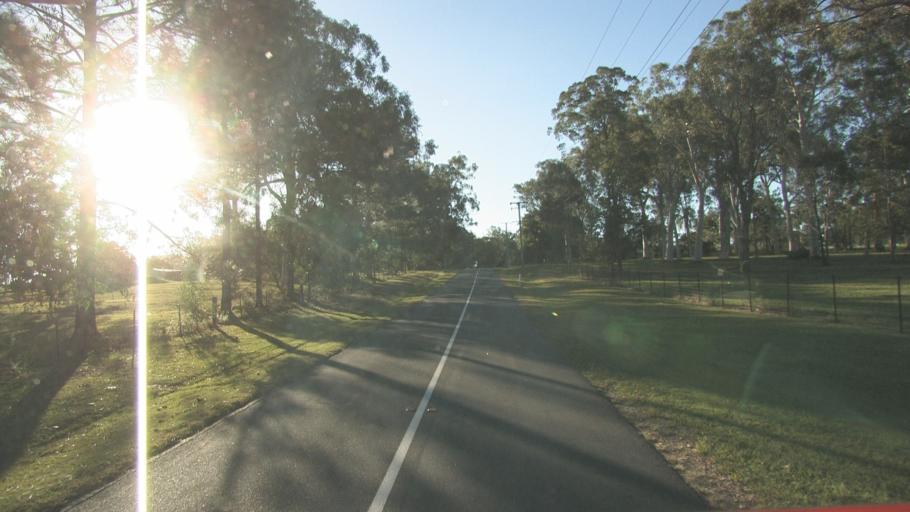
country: AU
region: Queensland
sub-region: Redland
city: Redland Bay
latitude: -27.6704
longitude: 153.2749
